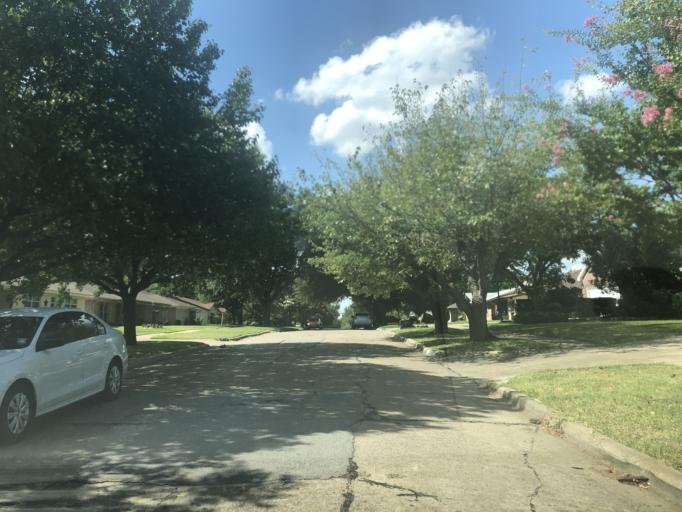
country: US
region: Texas
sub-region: Dallas County
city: Grand Prairie
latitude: 32.7348
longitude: -97.0026
